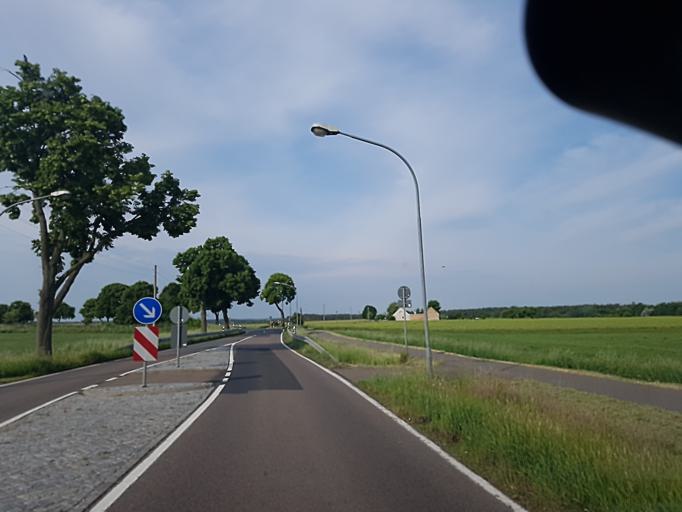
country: DE
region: Brandenburg
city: Niemegk
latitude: 52.0699
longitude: 12.6855
